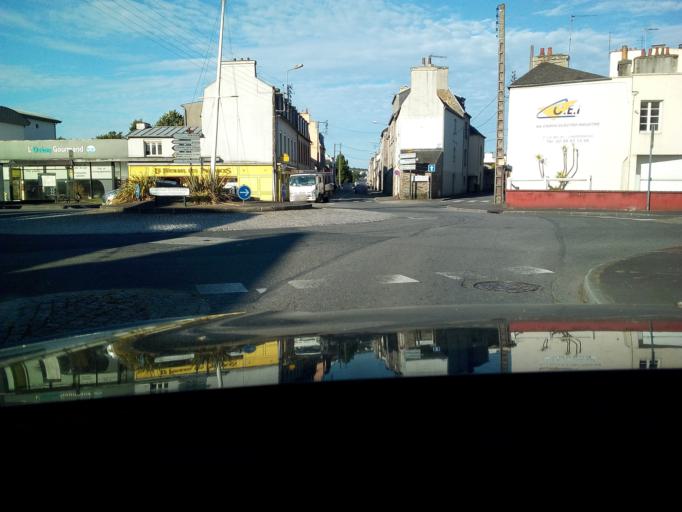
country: FR
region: Brittany
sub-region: Departement du Finistere
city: Landerneau
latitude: 48.4541
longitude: -4.2446
